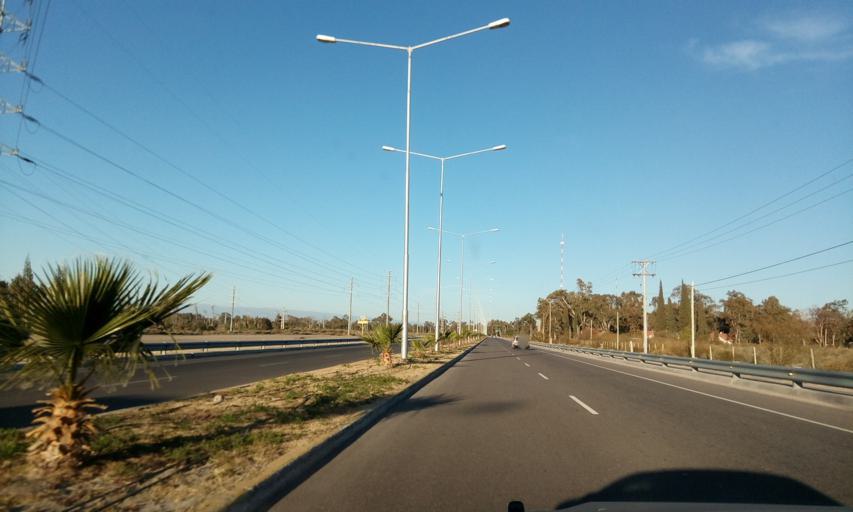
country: AR
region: San Juan
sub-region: Departamento de Rivadavia
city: Rivadavia
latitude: -31.5137
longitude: -68.6386
